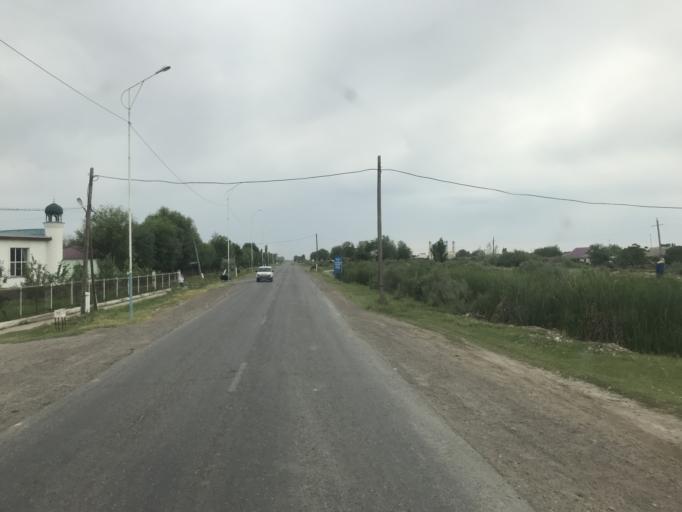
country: KZ
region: Ongtustik Qazaqstan
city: Asykata
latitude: 40.9331
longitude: 68.4087
